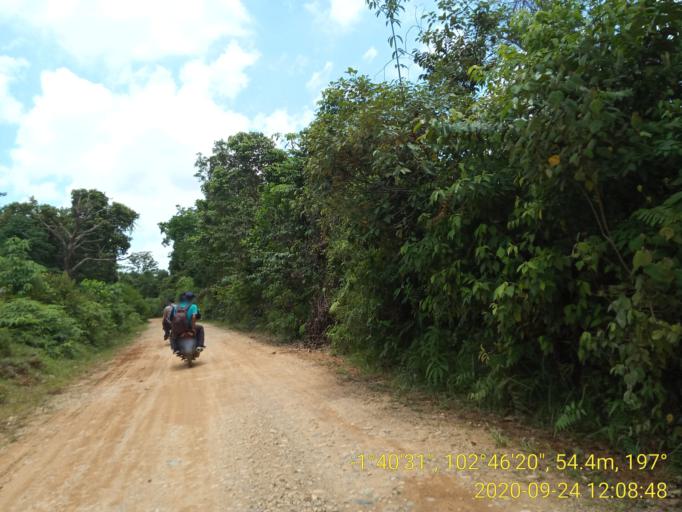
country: ID
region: Jambi
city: Sungaibengkal
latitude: -1.6753
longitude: 102.7724
